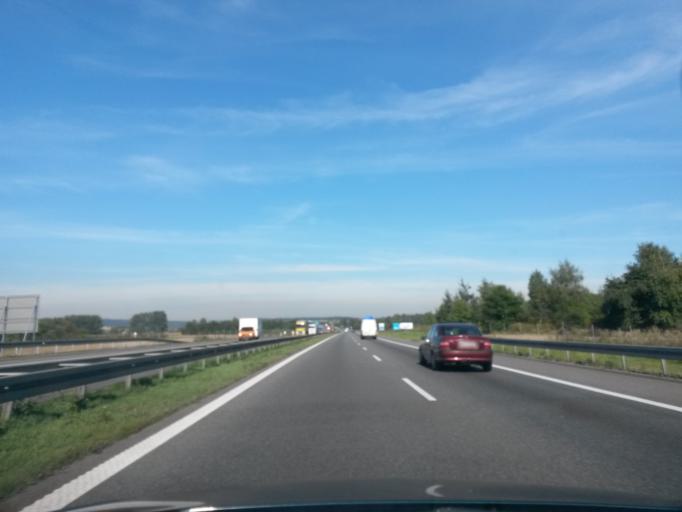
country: PL
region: Lesser Poland Voivodeship
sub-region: Powiat krakowski
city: Kryspinow
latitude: 50.0634
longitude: 19.8098
